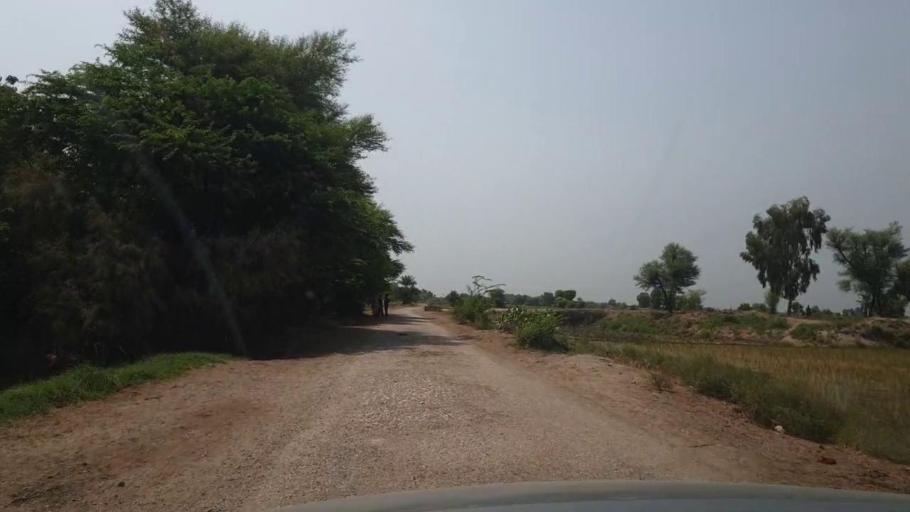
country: PK
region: Sindh
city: Madeji
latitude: 27.8032
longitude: 68.5383
